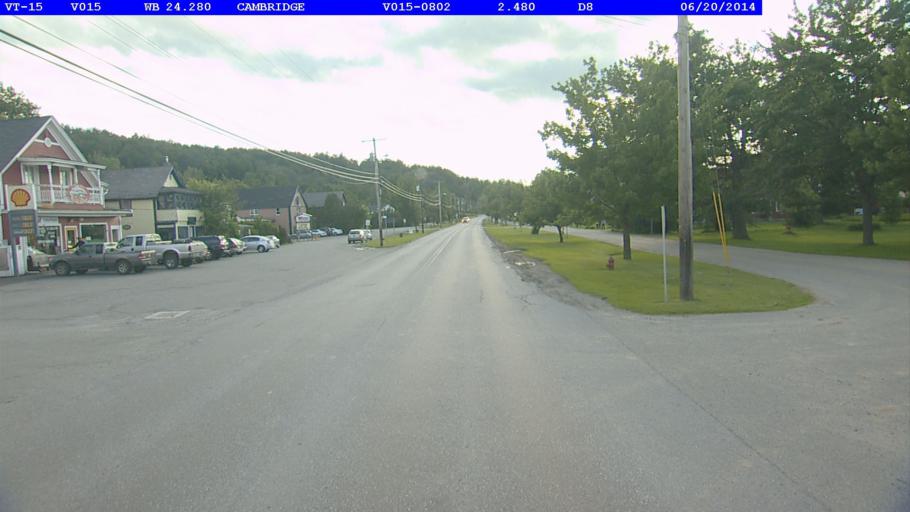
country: US
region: Vermont
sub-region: Chittenden County
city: Jericho
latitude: 44.6449
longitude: -72.8763
